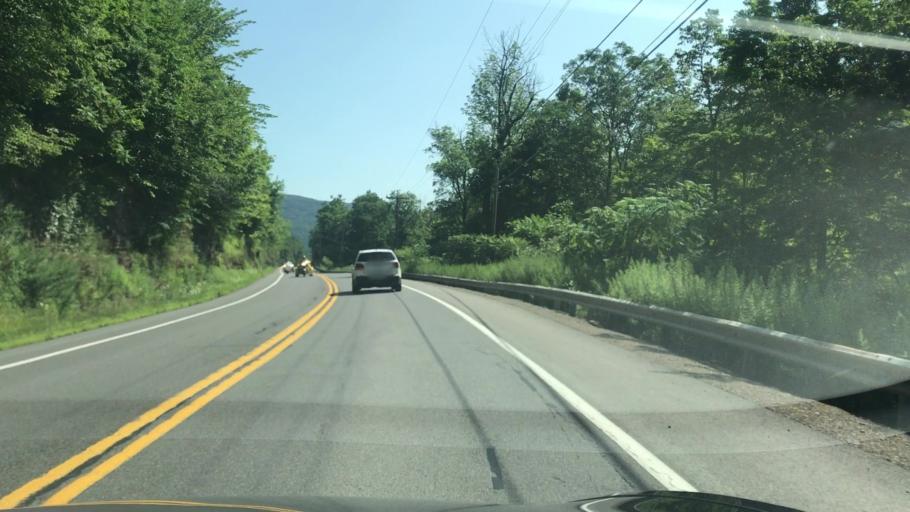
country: US
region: Pennsylvania
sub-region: Lycoming County
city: Kenmar
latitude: 41.4370
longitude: -76.9962
